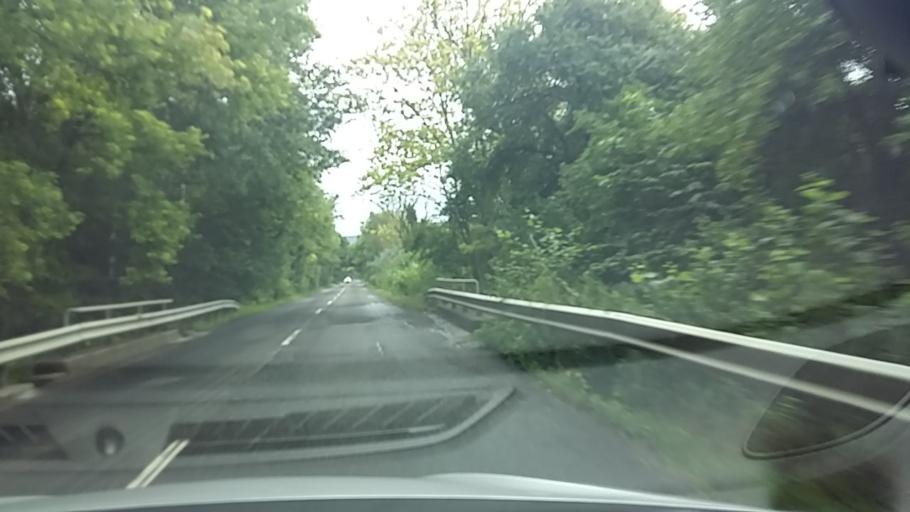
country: HU
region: Komarom-Esztergom
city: Esztergom
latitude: 47.8759
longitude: 18.7841
